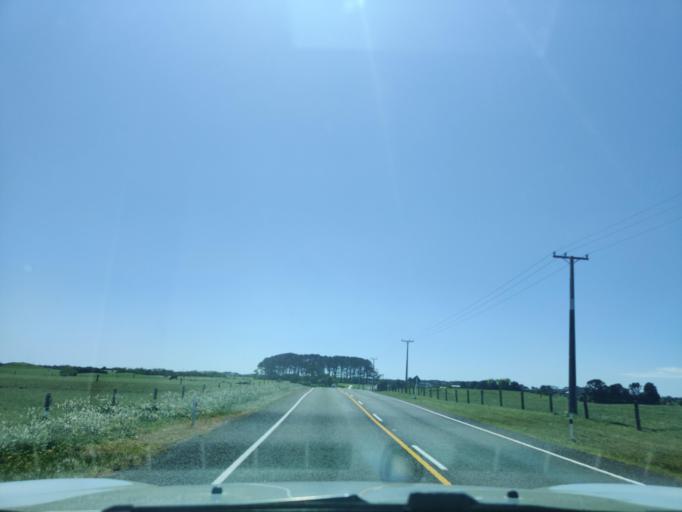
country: NZ
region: Taranaki
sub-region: South Taranaki District
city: Opunake
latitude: -39.3842
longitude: 173.8115
